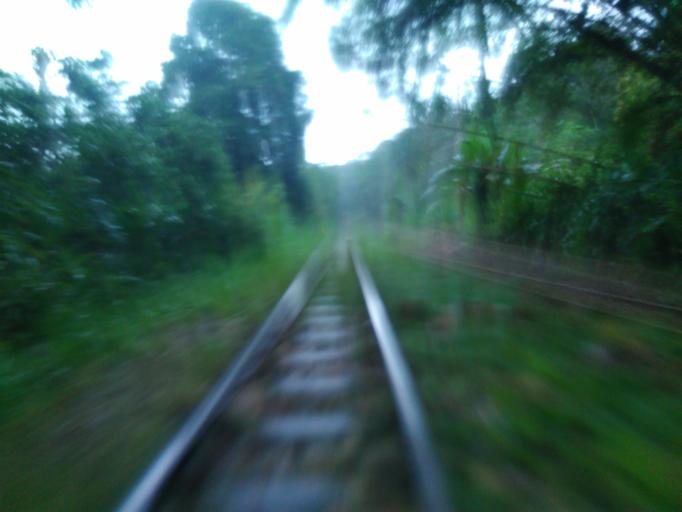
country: CO
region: Valle del Cauca
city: Buenaventura
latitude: 3.8497
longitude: -76.8604
